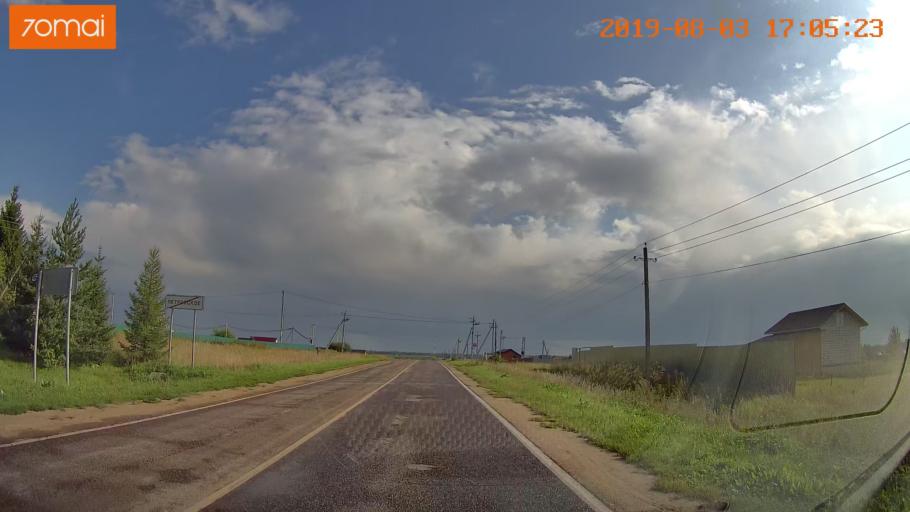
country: RU
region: Moskovskaya
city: Troitskoye
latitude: 55.3215
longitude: 38.5504
